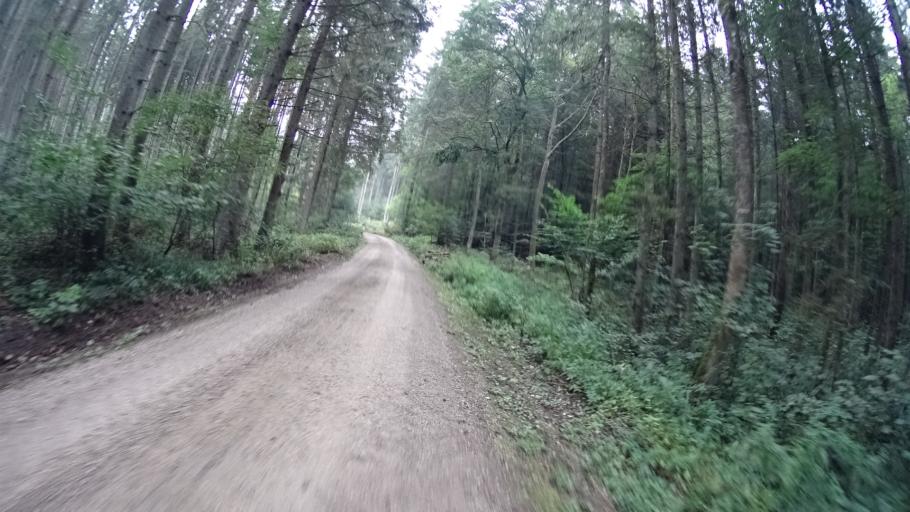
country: DE
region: Bavaria
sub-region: Upper Bavaria
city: Stammham
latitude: 48.8488
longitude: 11.4933
